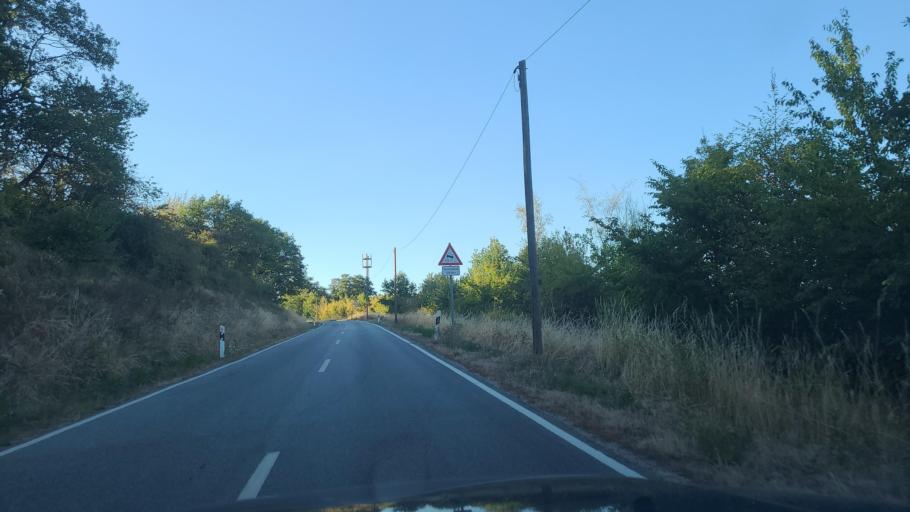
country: DE
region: Rheinland-Pfalz
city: Thornich
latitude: 49.8537
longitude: 6.8305
